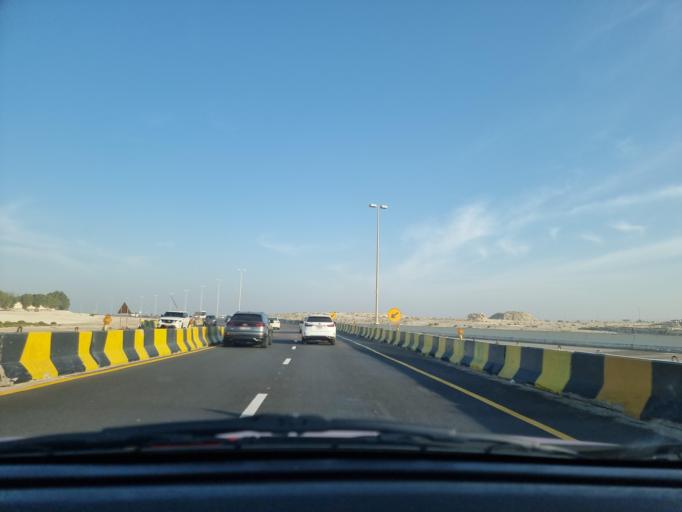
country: AE
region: Abu Dhabi
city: Abu Dhabi
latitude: 24.4700
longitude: 54.6711
